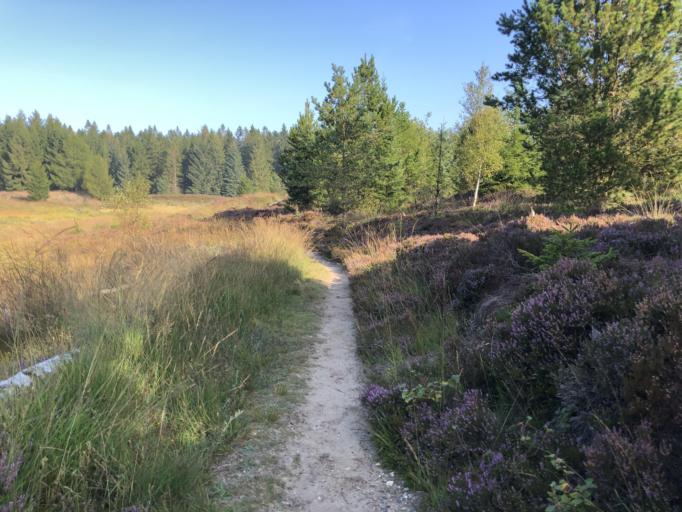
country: DK
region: Central Jutland
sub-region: Lemvig Kommune
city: Lemvig
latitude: 56.4759
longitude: 8.3334
